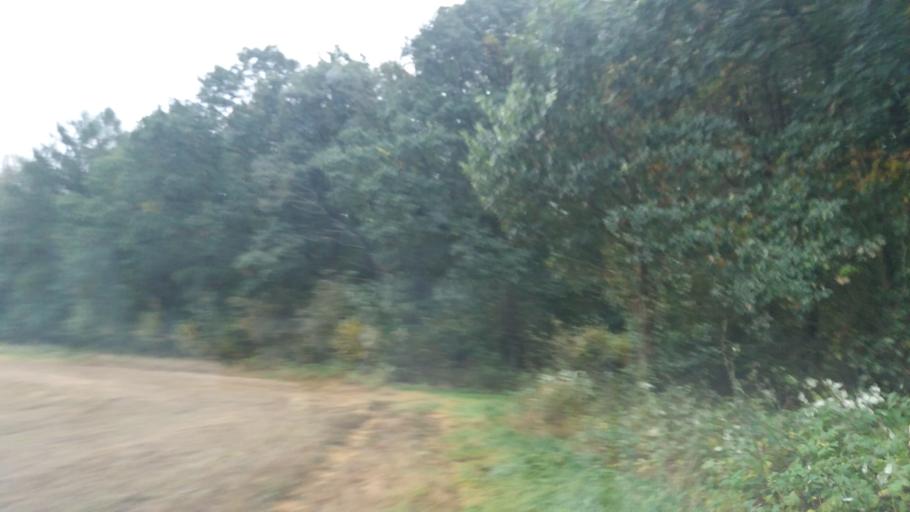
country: PL
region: West Pomeranian Voivodeship
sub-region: Powiat choszczenski
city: Pelczyce
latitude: 53.0704
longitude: 15.3008
